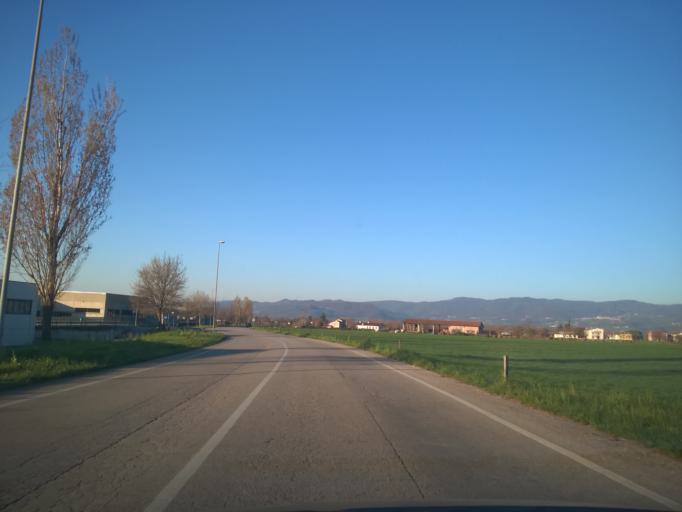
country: IT
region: Veneto
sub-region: Provincia di Vicenza
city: Thiene
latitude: 45.6914
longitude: 11.4629
